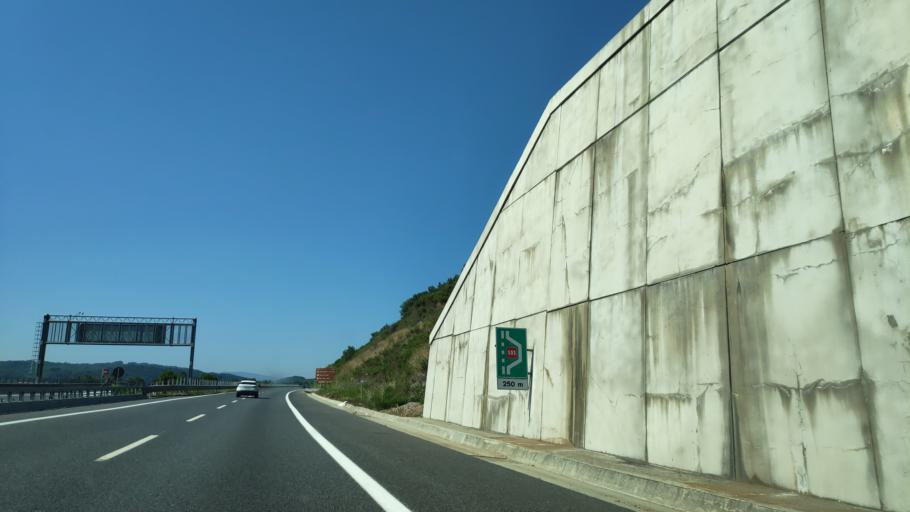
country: IT
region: Calabria
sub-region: Provincia di Reggio Calabria
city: Seminara
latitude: 38.3456
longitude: 15.8693
